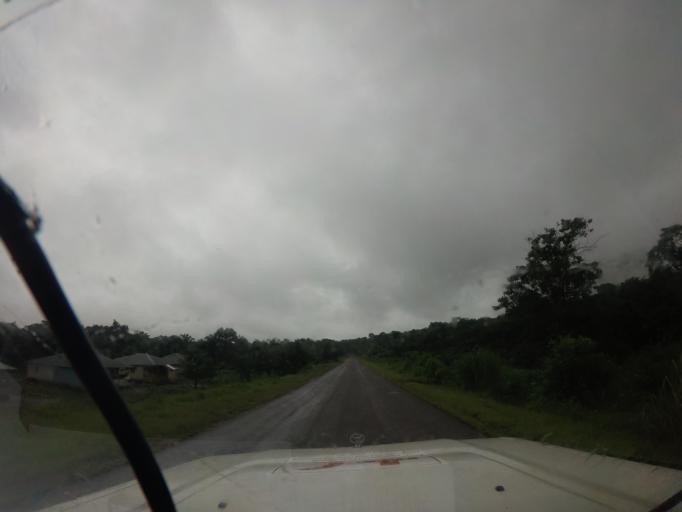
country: SL
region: Northern Province
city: Bumbuna
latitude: 9.2877
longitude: -11.9542
